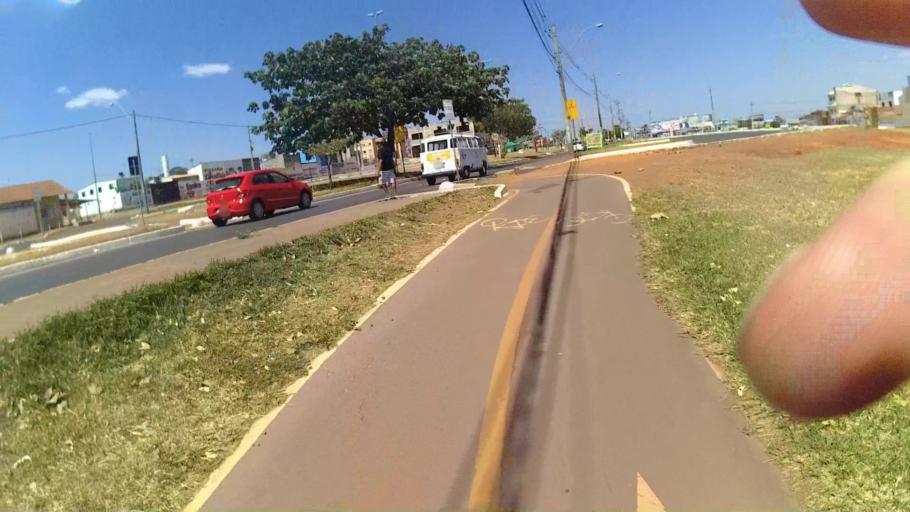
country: BR
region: Federal District
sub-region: Brasilia
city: Brasilia
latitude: -15.8990
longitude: -48.0490
